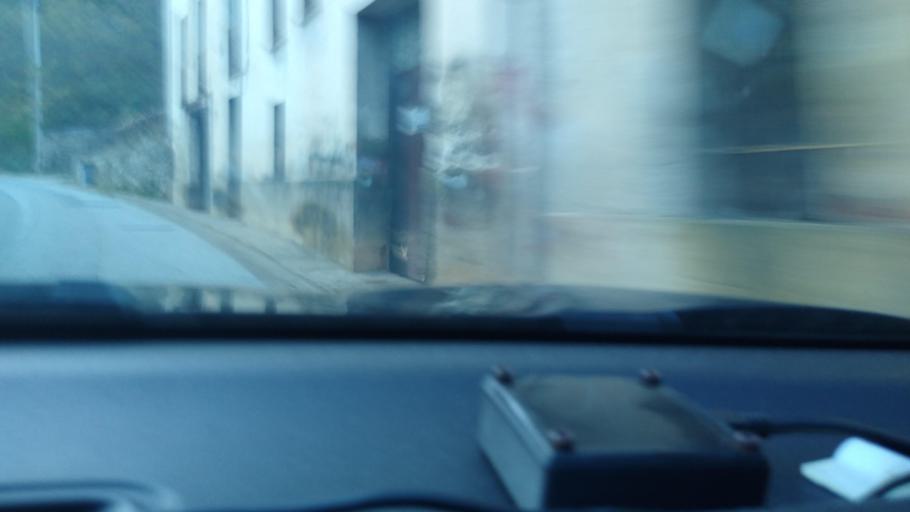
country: ES
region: Catalonia
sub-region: Provincia de Girona
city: Llivia
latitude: 42.5121
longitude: 2.1807
